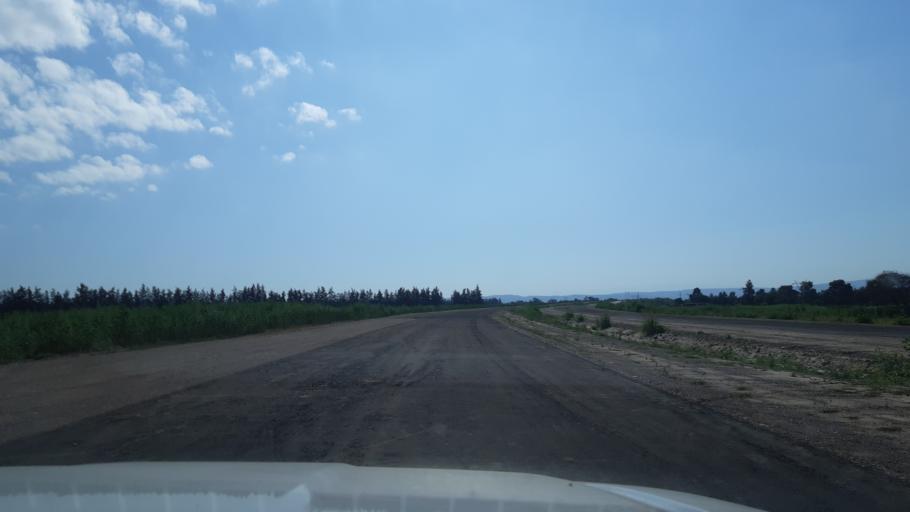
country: AR
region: Salta
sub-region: Departamento de General Guemes
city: General Martin Miguel de Guemes
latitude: -24.5280
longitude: -65.0775
